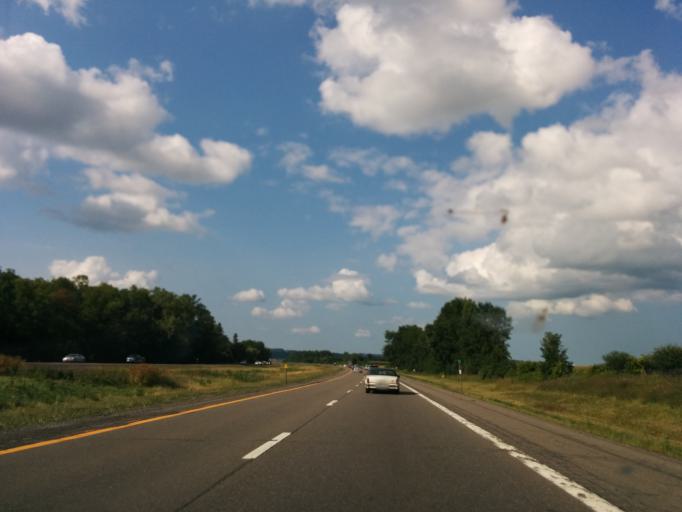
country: US
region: New York
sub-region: Cortland County
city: Homer
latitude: 42.7682
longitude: -76.1293
